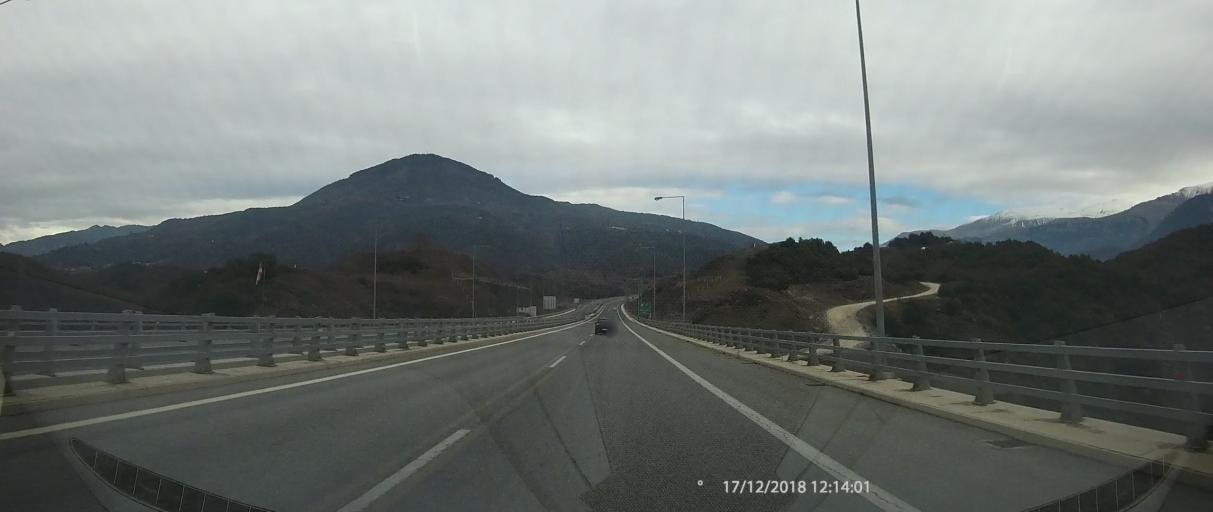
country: GR
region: Epirus
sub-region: Nomos Ioanninon
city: Katsikas
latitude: 39.7139
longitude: 20.9861
